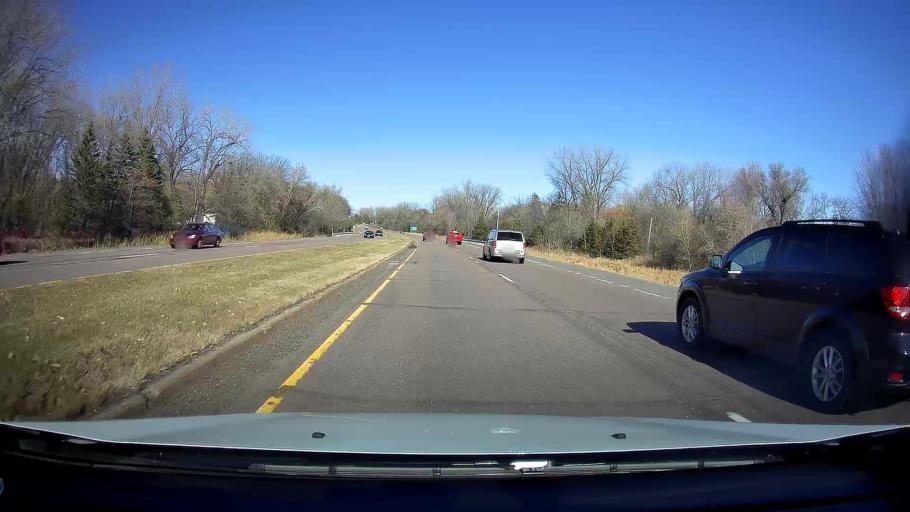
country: US
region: Minnesota
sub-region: Ramsey County
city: Arden Hills
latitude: 45.0410
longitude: -93.1578
